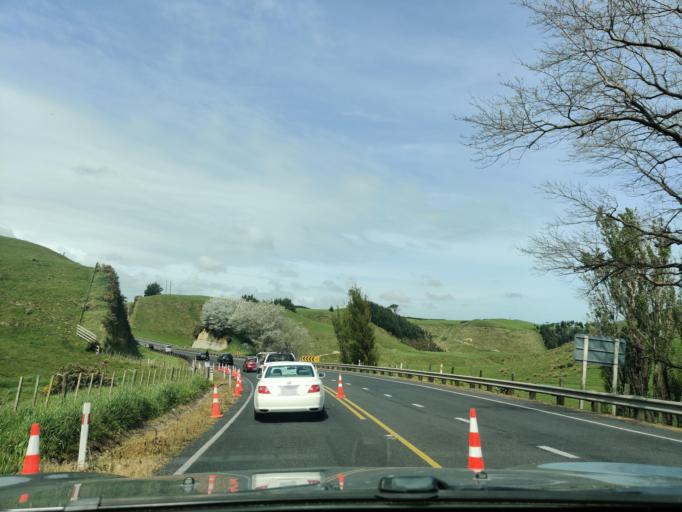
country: NZ
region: Taranaki
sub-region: South Taranaki District
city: Hawera
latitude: -39.6179
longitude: 174.3419
